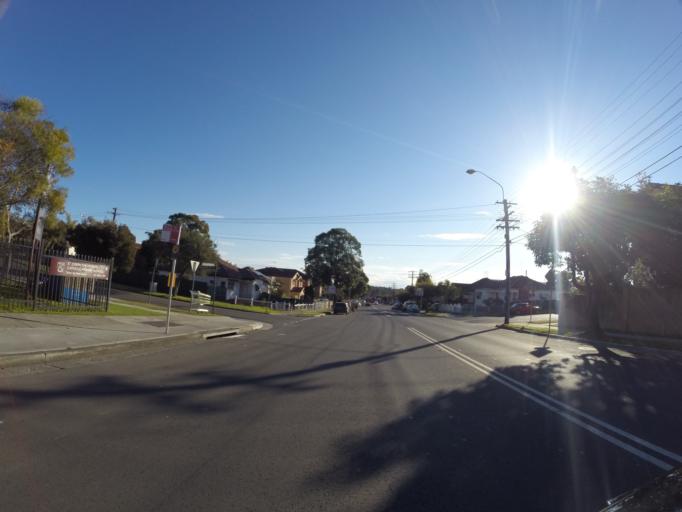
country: AU
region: New South Wales
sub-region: Auburn
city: Berala
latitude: -33.8645
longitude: 151.0242
